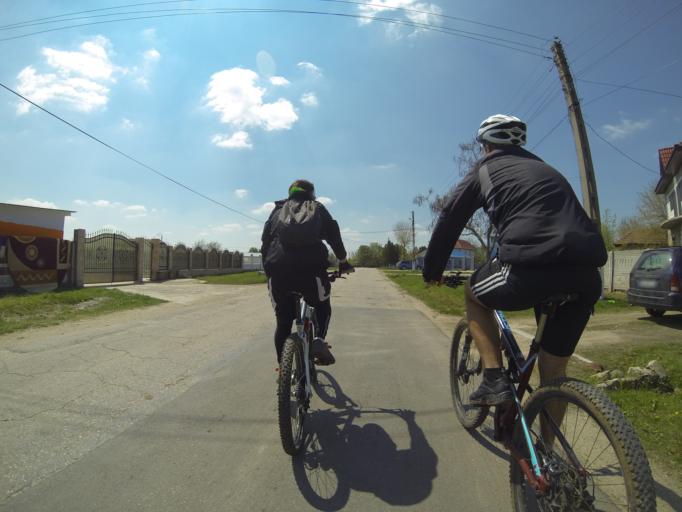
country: RO
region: Dolj
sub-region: Comuna Salcuta
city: Salcuta
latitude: 44.2518
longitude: 23.4193
